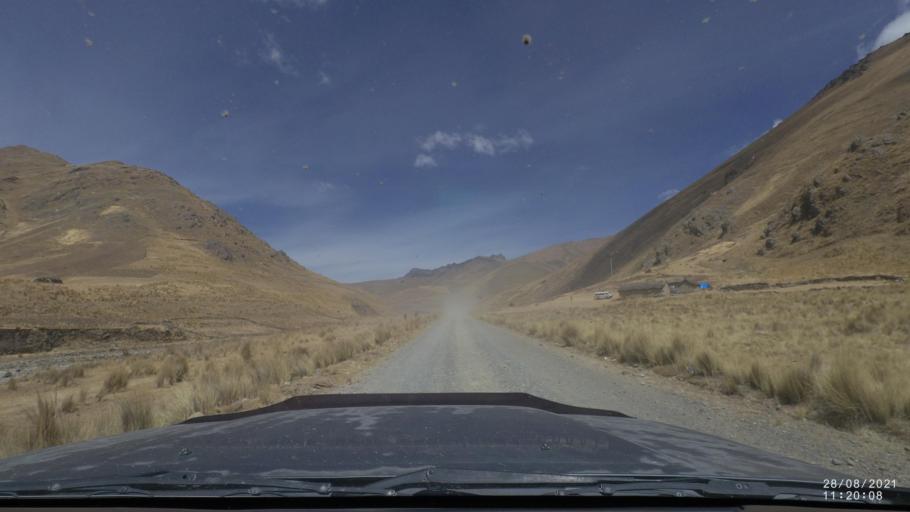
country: BO
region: Cochabamba
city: Cochabamba
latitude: -17.1566
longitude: -66.3382
